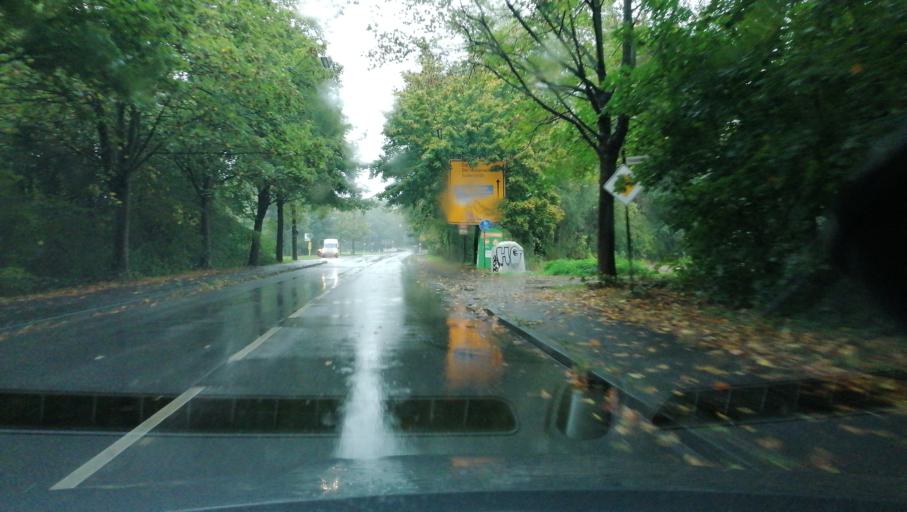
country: DE
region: North Rhine-Westphalia
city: Oer-Erkenschwick
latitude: 51.5890
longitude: 7.2564
